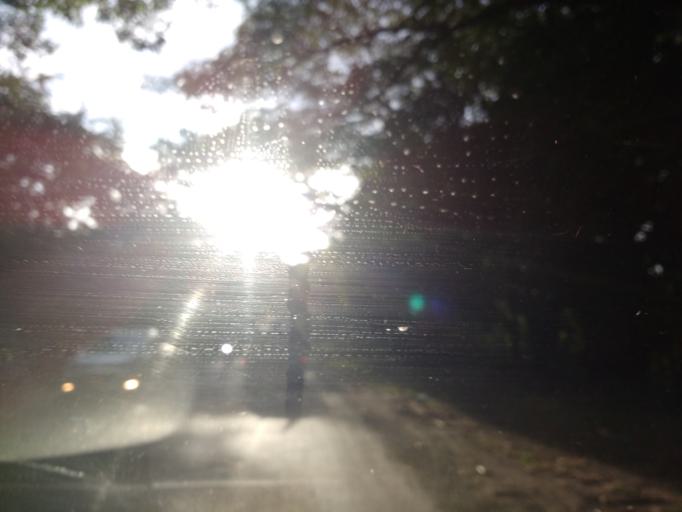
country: CO
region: Valle del Cauca
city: Ansermanuevo
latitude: 4.7771
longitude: -75.9626
